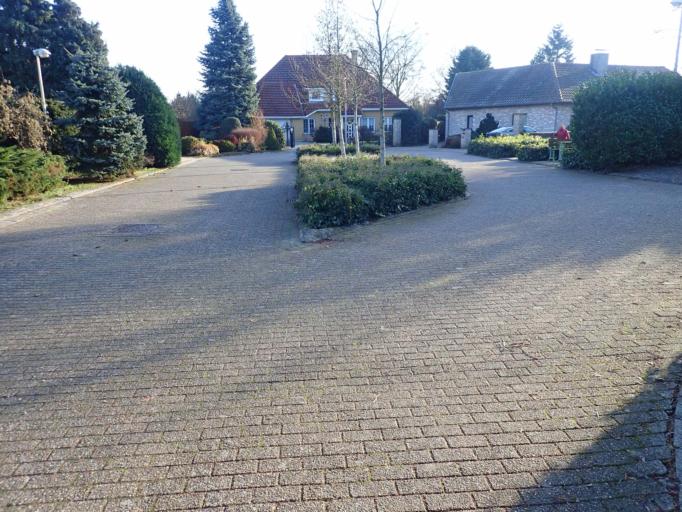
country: BE
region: Flanders
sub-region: Provincie Antwerpen
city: Essen
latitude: 51.4527
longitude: 4.4471
